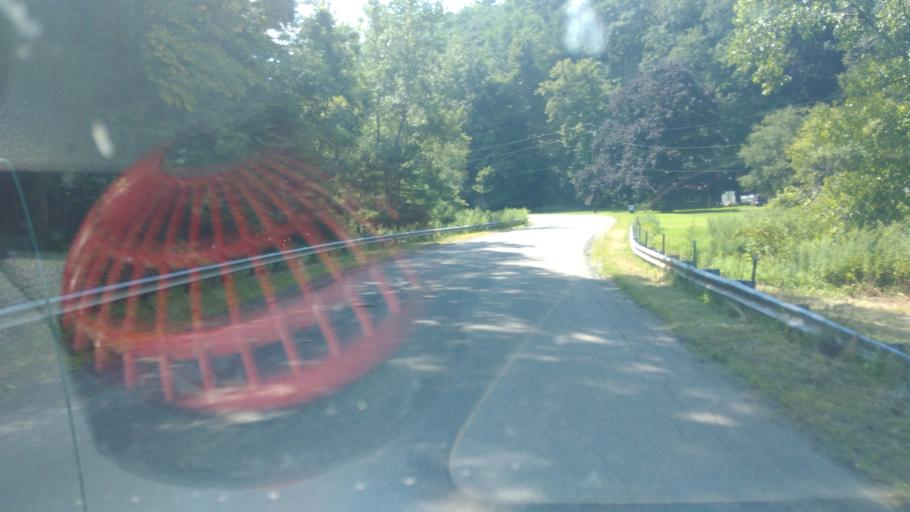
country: US
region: New York
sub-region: Steuben County
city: Canisteo
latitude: 42.3026
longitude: -77.6093
